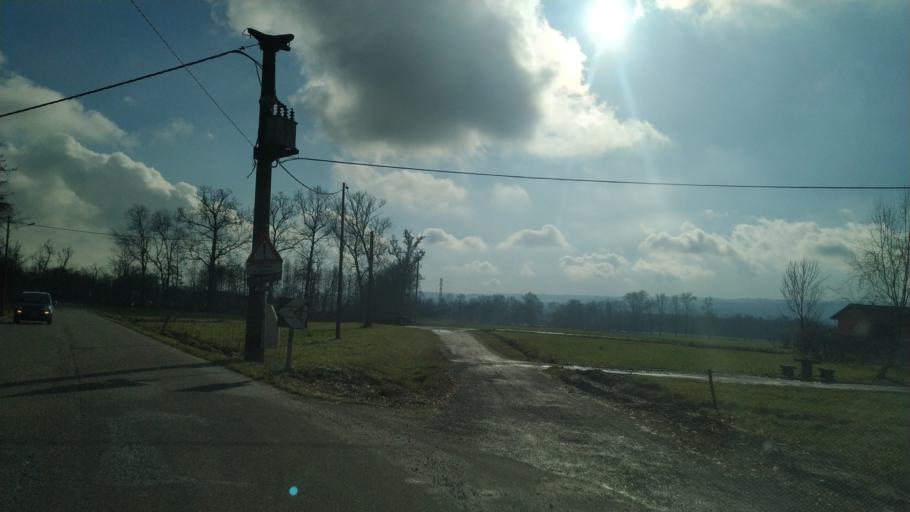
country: IT
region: Piedmont
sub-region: Provincia di Biella
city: Occhieppo Inferiore
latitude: 45.5365
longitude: 8.0253
